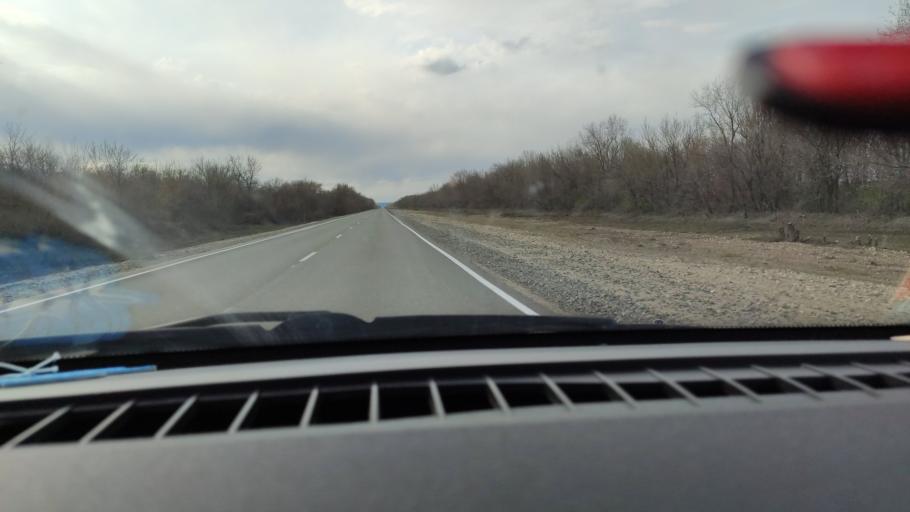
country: RU
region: Saratov
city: Privolzhskiy
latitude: 51.1649
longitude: 45.9486
